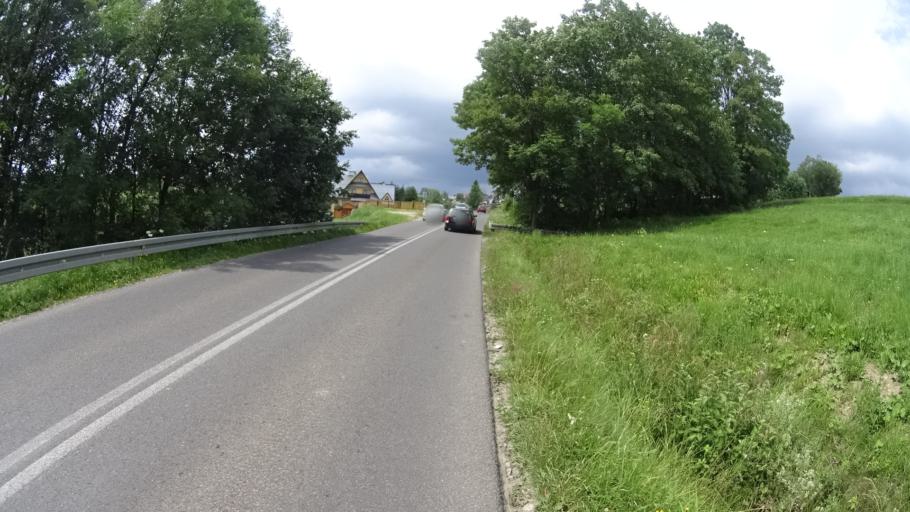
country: PL
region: Lesser Poland Voivodeship
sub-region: Powiat tatrzanski
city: Zakopane
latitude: 49.3380
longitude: 19.9595
